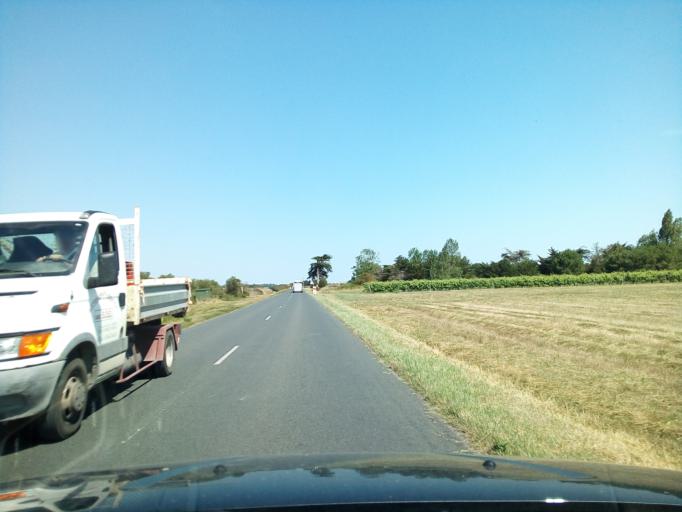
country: FR
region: Poitou-Charentes
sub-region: Departement de la Charente-Maritime
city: Boyard-Ville
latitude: 45.9693
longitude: -1.2816
